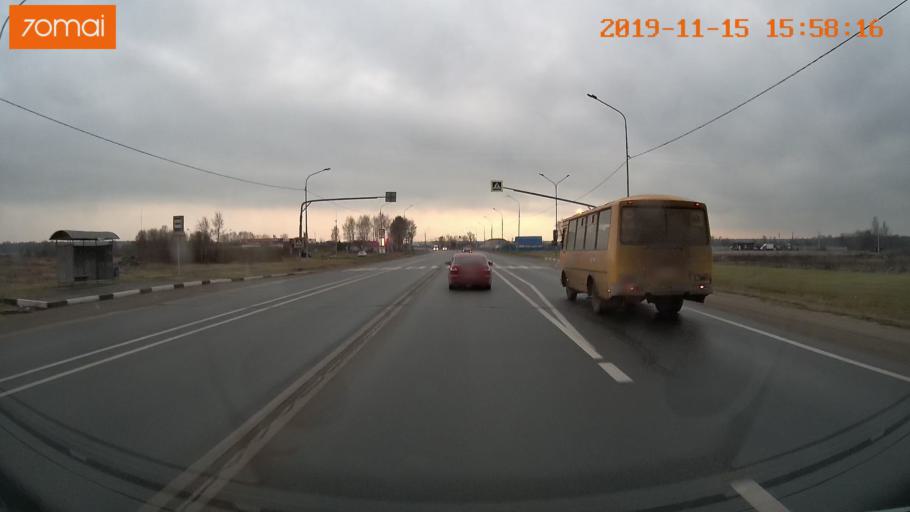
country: RU
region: Jaroslavl
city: Yaroslavl
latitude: 57.8220
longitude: 39.9564
